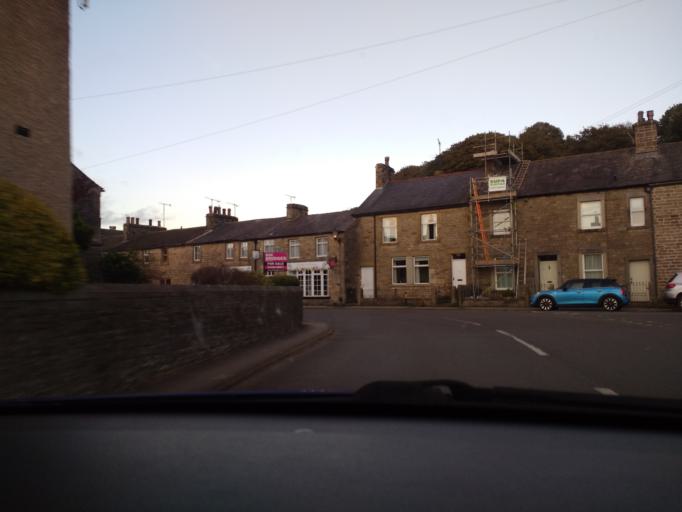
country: GB
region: England
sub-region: Lancashire
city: Caton
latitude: 54.1123
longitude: -2.6367
